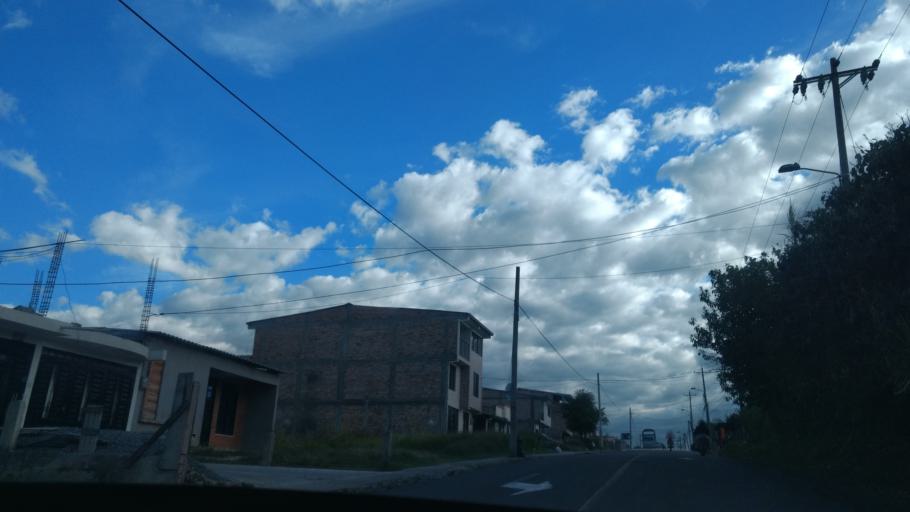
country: CO
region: Cauca
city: Popayan
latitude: 2.4852
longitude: -76.5773
